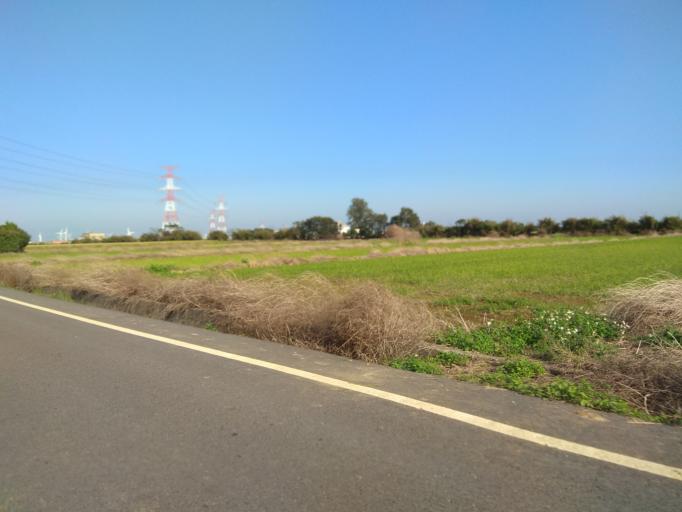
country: TW
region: Taiwan
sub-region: Hsinchu
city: Zhubei
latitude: 24.9967
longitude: 121.0621
